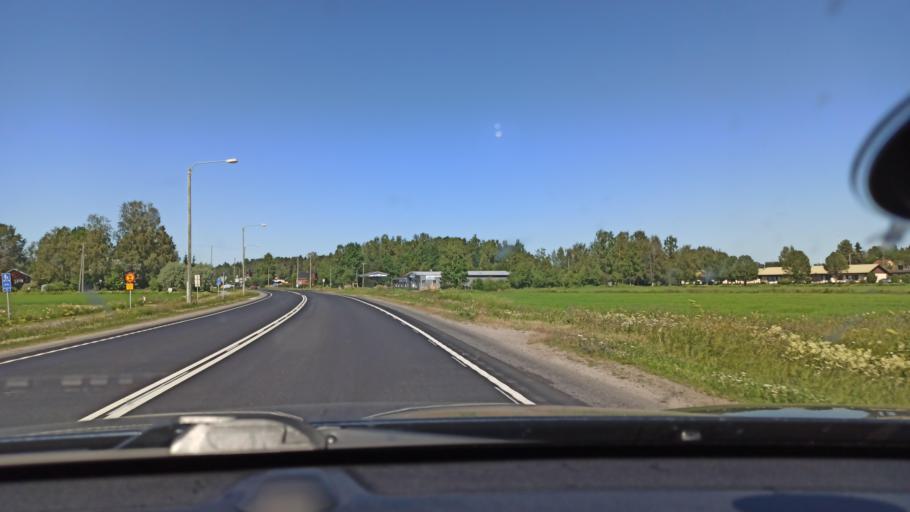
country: FI
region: Ostrobothnia
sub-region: Vaasa
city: Oravais
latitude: 63.3091
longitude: 22.3878
